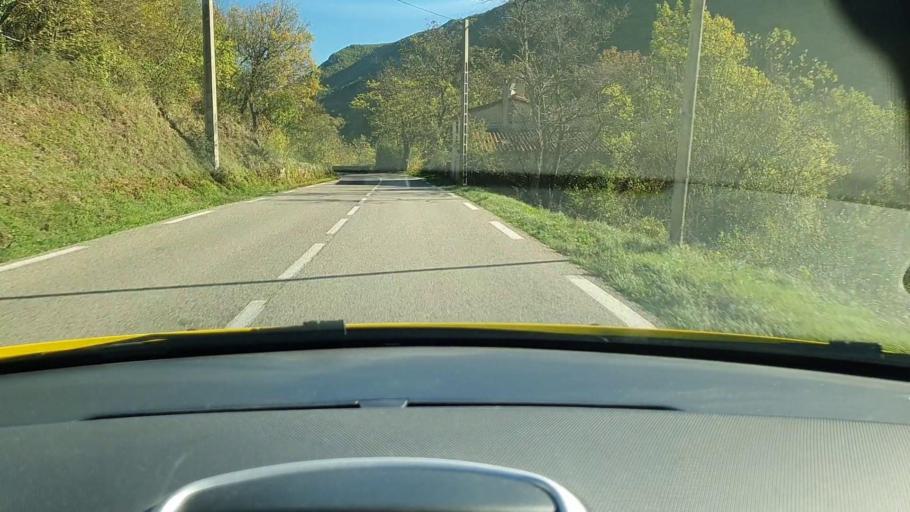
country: FR
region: Languedoc-Roussillon
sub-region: Departement du Gard
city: Aveze
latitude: 43.9707
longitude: 3.5549
